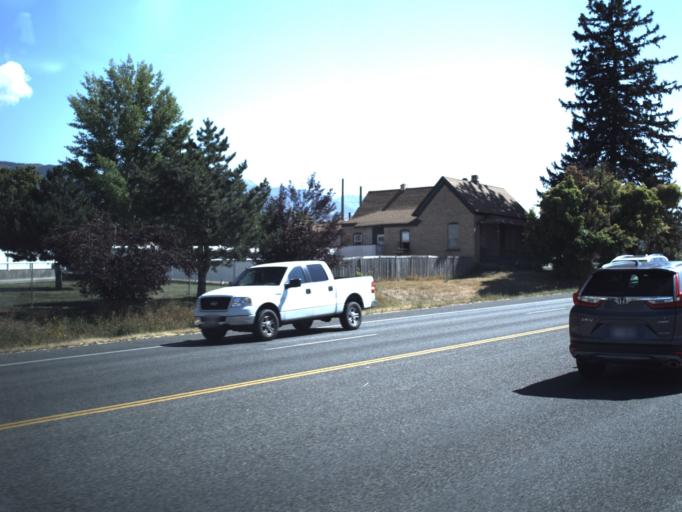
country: US
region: Utah
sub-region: Cache County
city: Richmond
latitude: 41.9256
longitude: -111.8144
